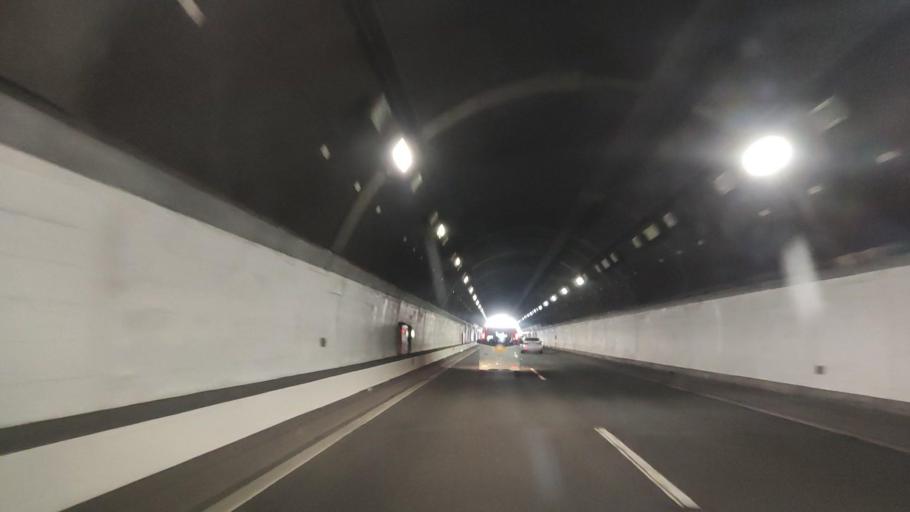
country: JP
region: Hyogo
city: Himeji
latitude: 34.8201
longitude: 134.6428
